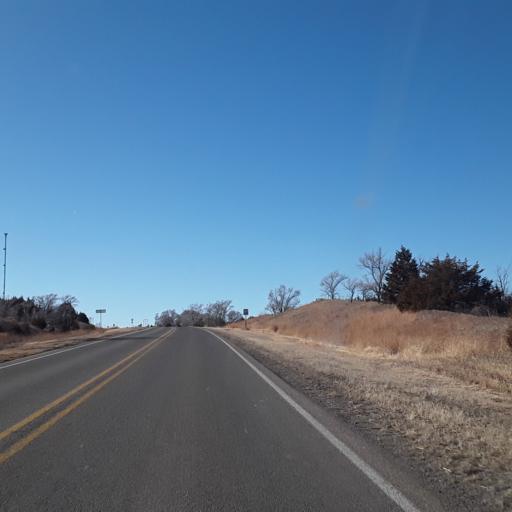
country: US
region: Nebraska
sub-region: Frontier County
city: Stockville
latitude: 40.6576
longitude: -100.6274
